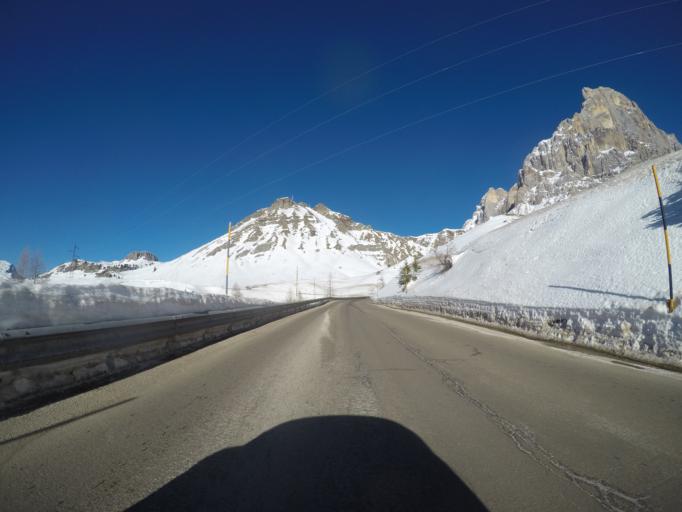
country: IT
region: Veneto
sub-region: Provincia di Belluno
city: Falcade Alto
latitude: 46.2871
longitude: 11.7956
